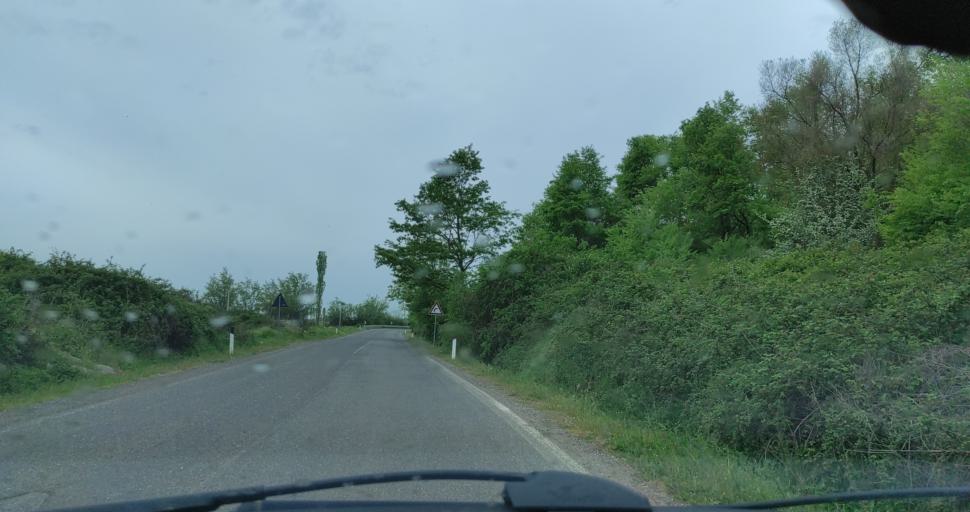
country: AL
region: Lezhe
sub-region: Rrethi i Kurbinit
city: Mamurras
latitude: 41.5906
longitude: 19.7002
